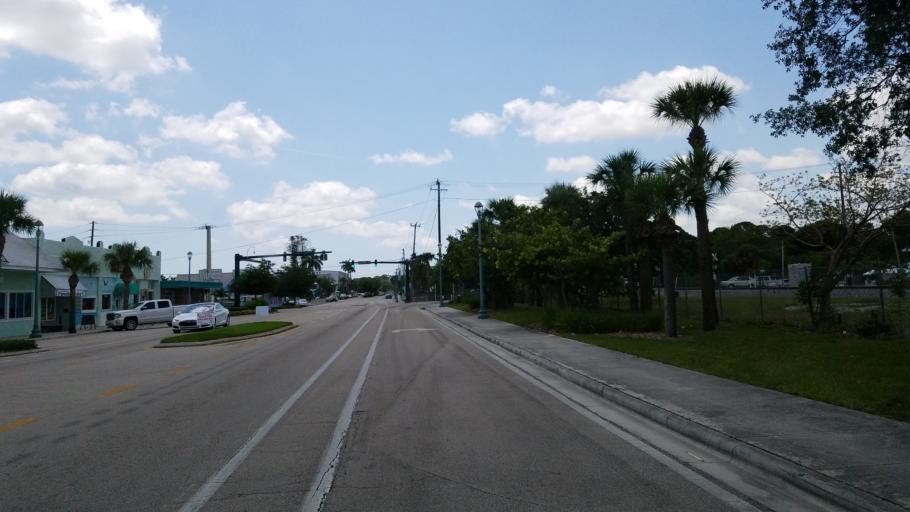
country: US
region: Florida
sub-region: Martin County
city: Port Salerno
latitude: 27.1465
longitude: -80.1983
